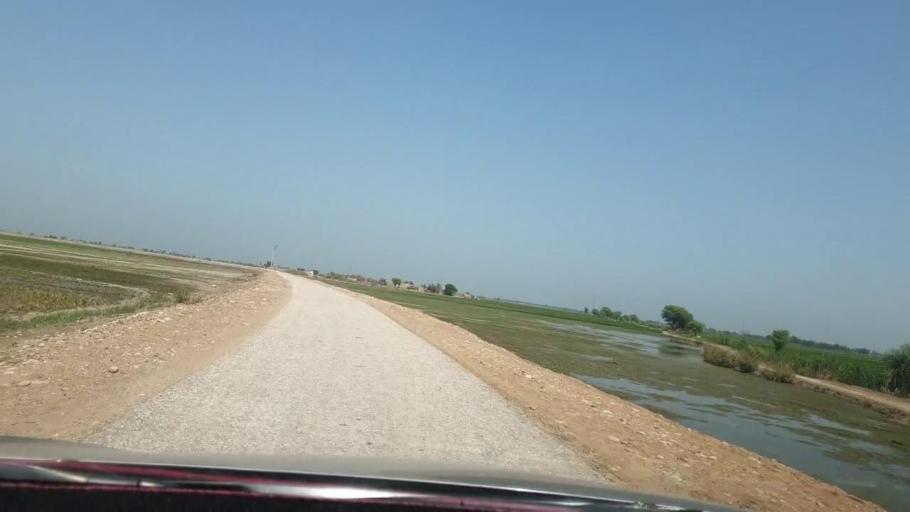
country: PK
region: Sindh
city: Warah
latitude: 27.5614
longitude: 67.7499
